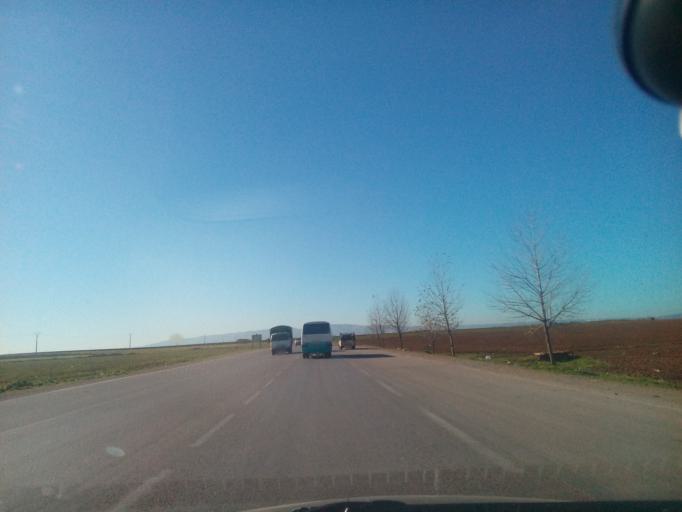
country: DZ
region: Relizane
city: Relizane
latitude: 35.8934
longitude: 0.6421
